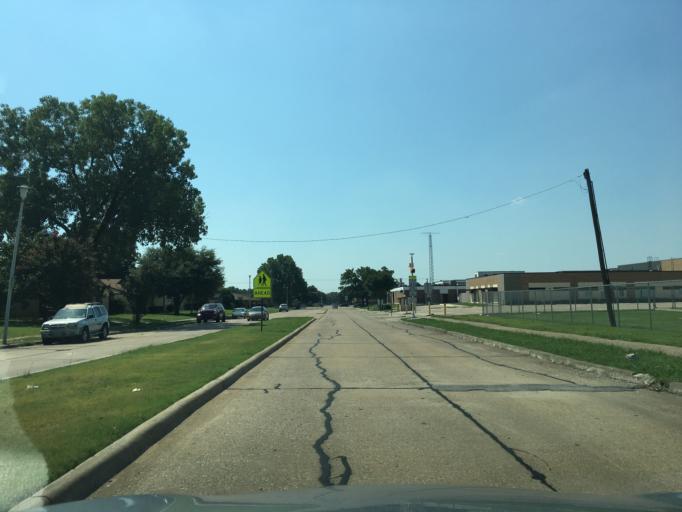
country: US
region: Texas
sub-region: Dallas County
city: Garland
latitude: 32.9333
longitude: -96.6573
